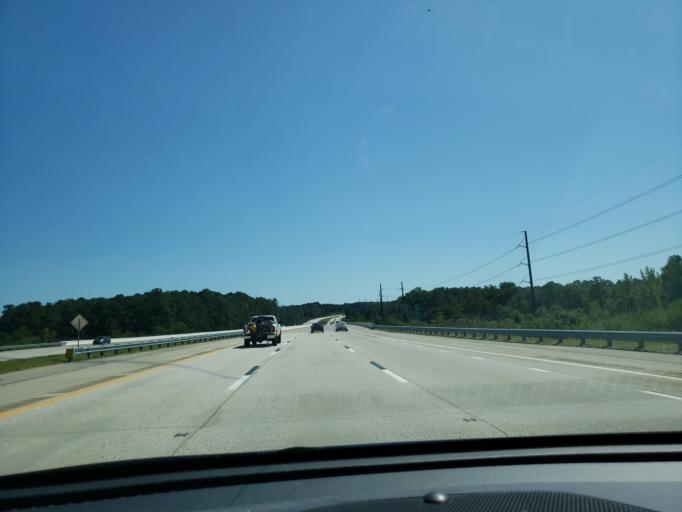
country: US
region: North Carolina
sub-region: Wake County
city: Green Level
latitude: 35.7795
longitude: -78.8857
